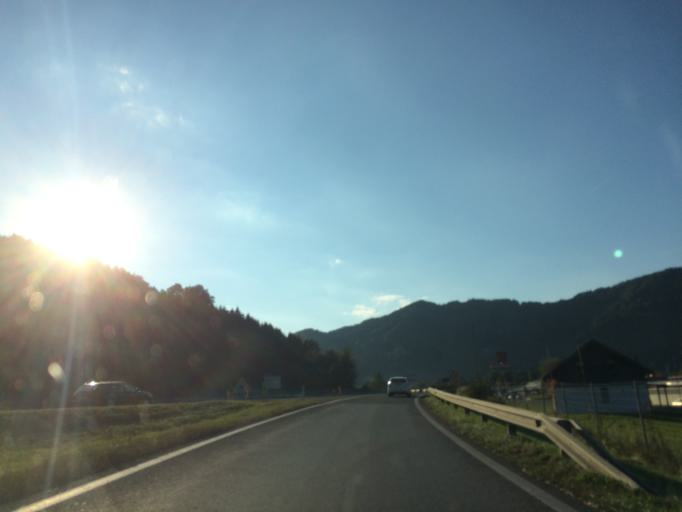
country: AT
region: Styria
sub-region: Politischer Bezirk Leoben
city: Leoben
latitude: 47.3540
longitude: 15.0796
